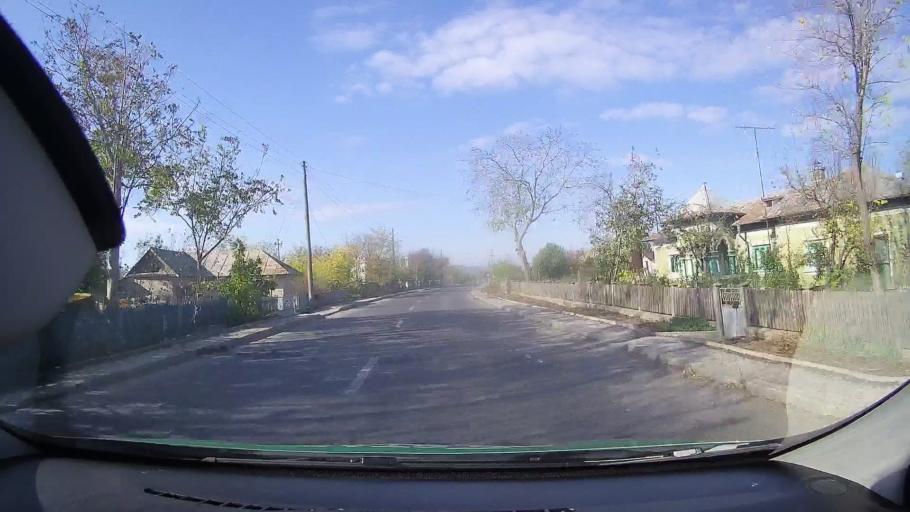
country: RO
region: Tulcea
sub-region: Comuna Valea Nucarilor
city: Iazurile
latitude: 45.0221
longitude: 28.9478
